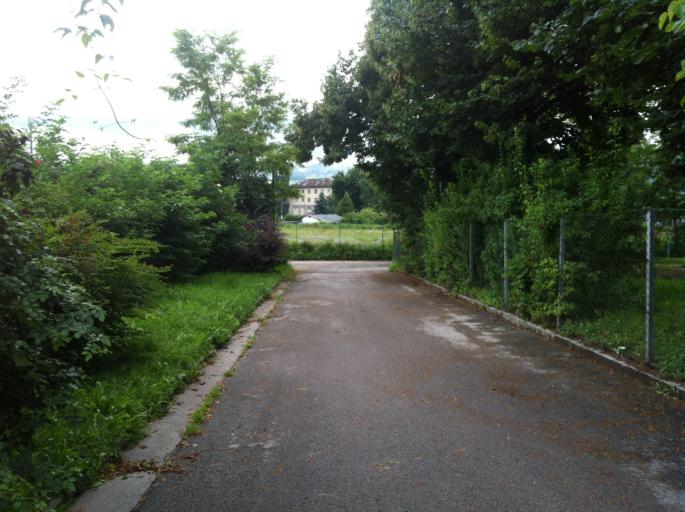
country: AT
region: Tyrol
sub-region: Politischer Bezirk Innsbruck Land
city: Ampass
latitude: 47.2728
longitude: 11.4260
